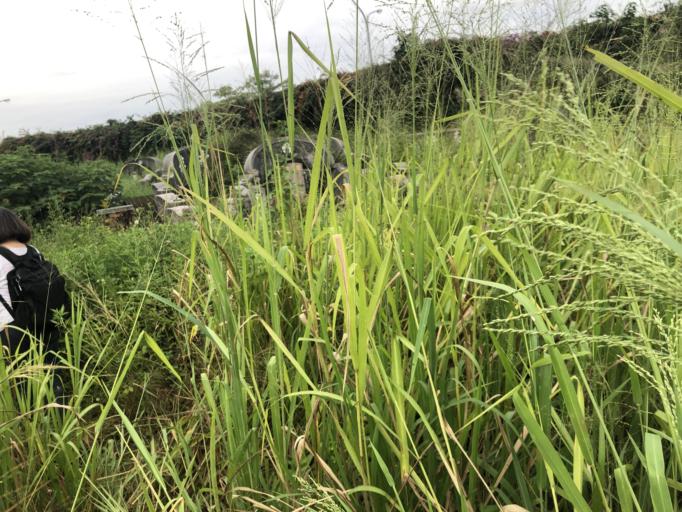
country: TW
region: Taiwan
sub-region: Tainan
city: Tainan
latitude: 22.9652
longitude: 120.1982
